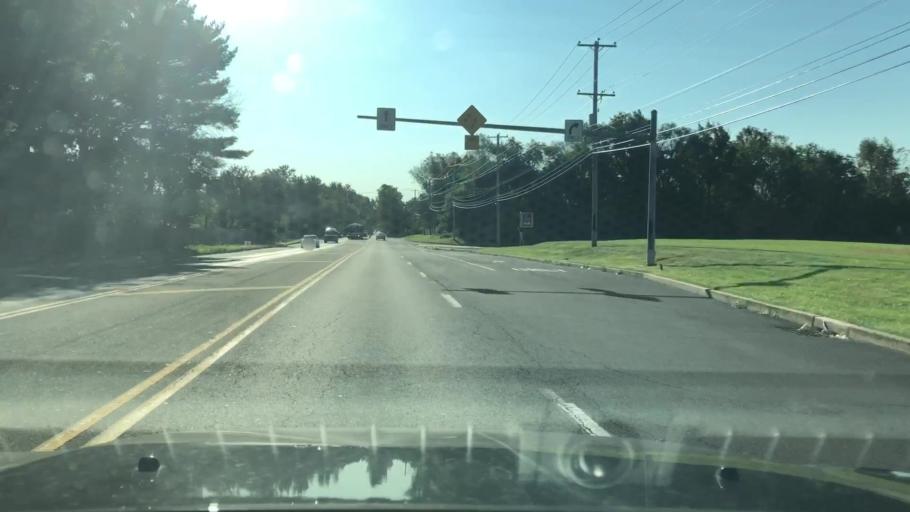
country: US
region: Pennsylvania
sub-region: Bucks County
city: Woodbourne
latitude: 40.1730
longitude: -74.8828
